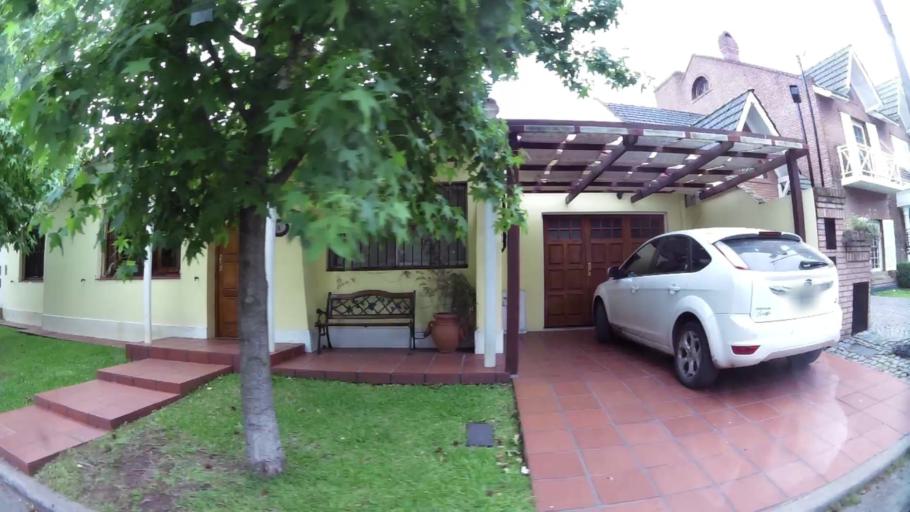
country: AR
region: Buenos Aires
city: San Justo
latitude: -34.7362
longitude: -58.5242
